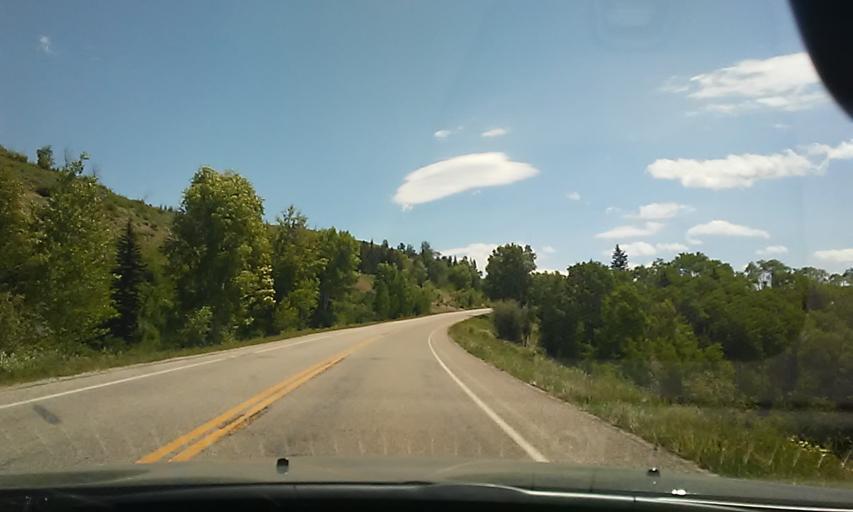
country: US
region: Wyoming
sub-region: Teton County
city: Jackson
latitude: 43.8390
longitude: -110.4908
